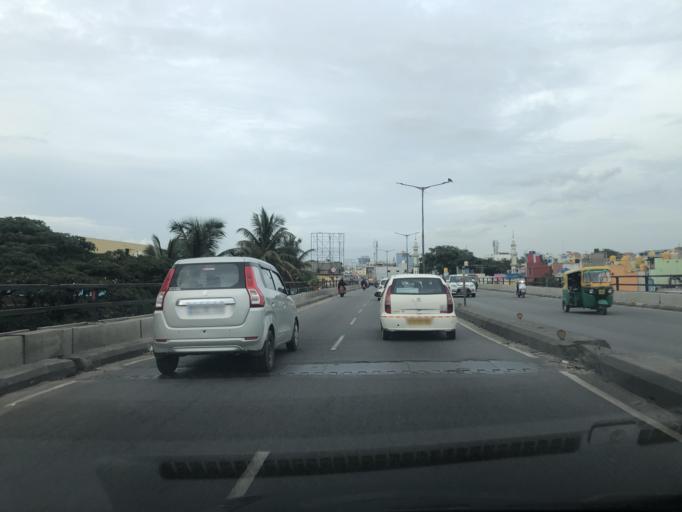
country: IN
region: Karnataka
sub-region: Bangalore Urban
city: Bangalore
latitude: 12.9628
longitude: 77.5657
